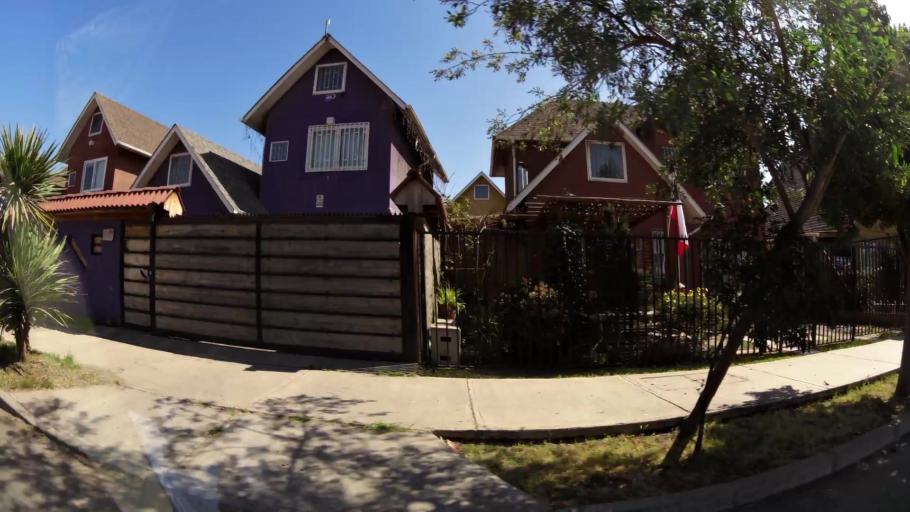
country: CL
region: Santiago Metropolitan
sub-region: Provincia de Chacabuco
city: Chicureo Abajo
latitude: -33.3255
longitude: -70.7429
